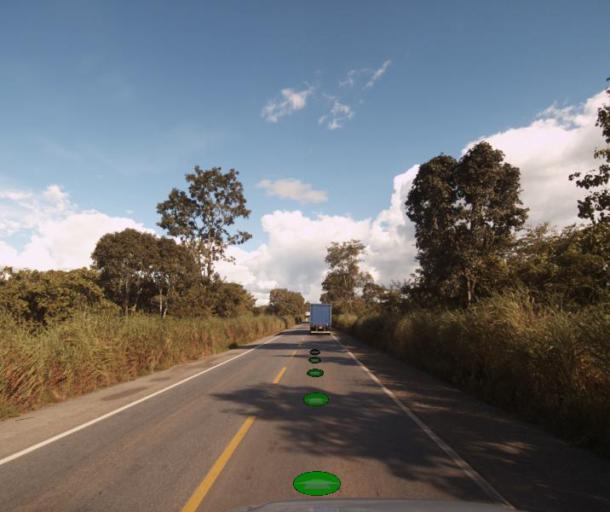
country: BR
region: Goias
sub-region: Porangatu
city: Porangatu
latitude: -13.1235
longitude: -49.1977
